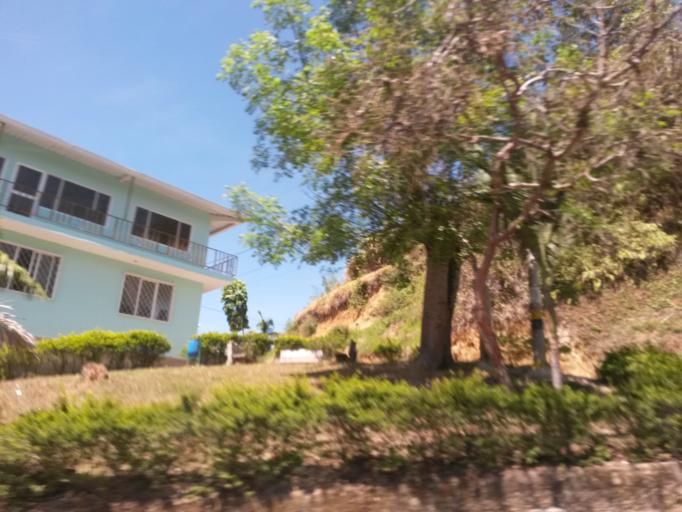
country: CO
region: Cauca
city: El Tambo
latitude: 2.4512
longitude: -76.8064
